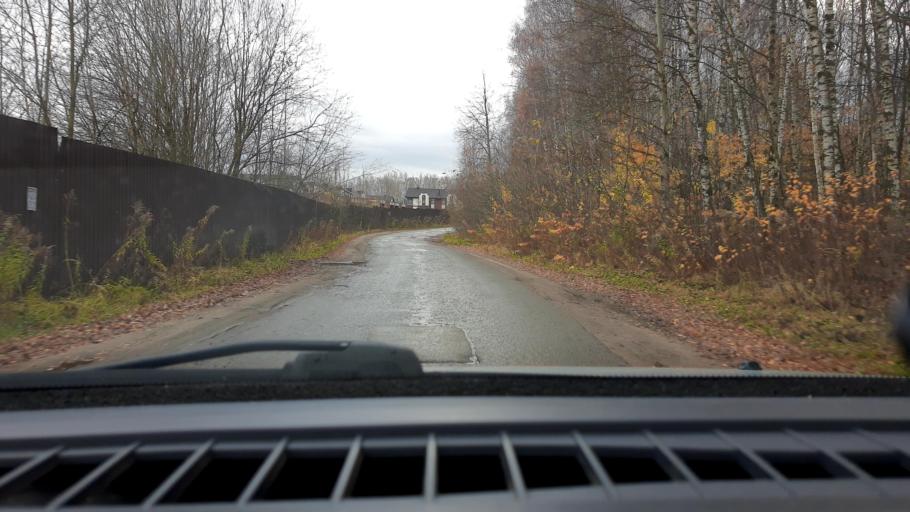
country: RU
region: Nizjnij Novgorod
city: Afonino
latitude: 56.1907
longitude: 44.1109
